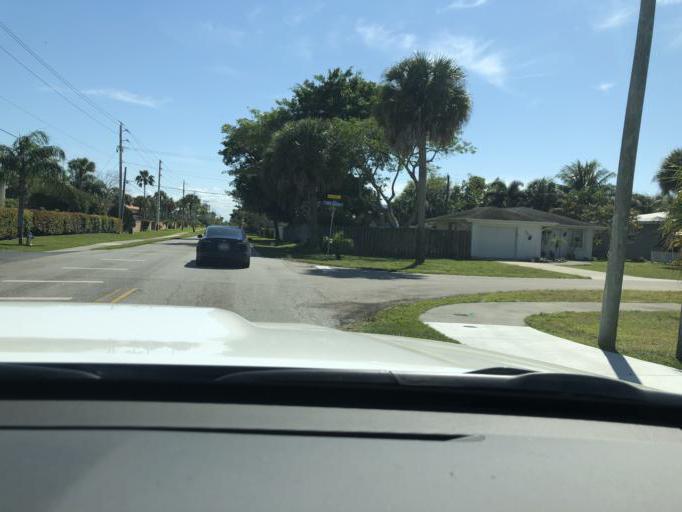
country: US
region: Florida
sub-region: Martin County
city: Stuart
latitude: 27.1819
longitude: -80.2571
